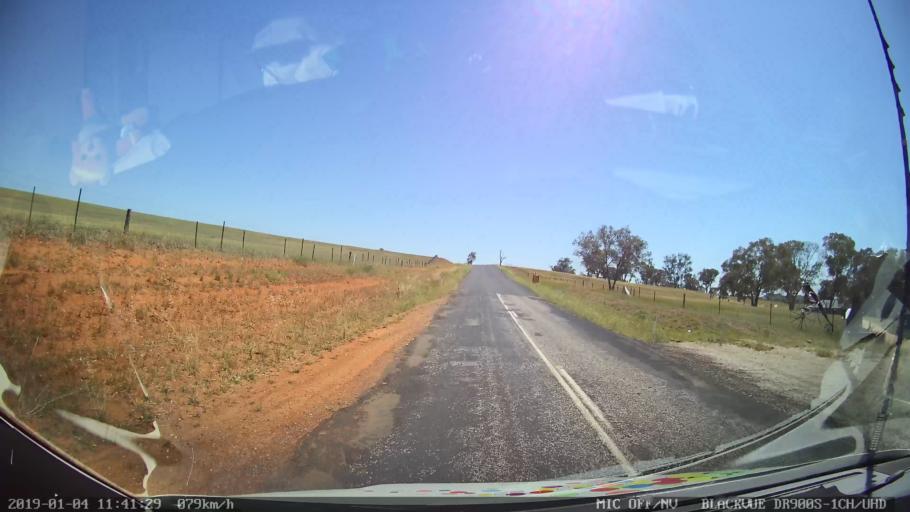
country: AU
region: New South Wales
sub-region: Cabonne
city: Molong
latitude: -32.9931
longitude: 148.7877
